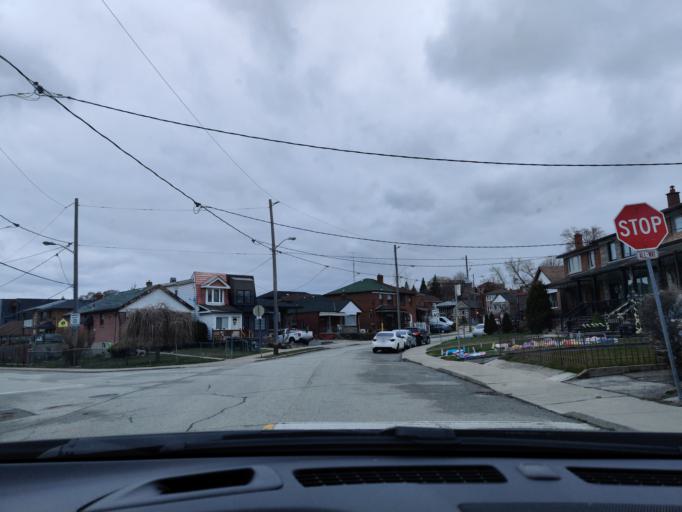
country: CA
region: Ontario
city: Toronto
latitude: 43.6893
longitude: -79.4494
